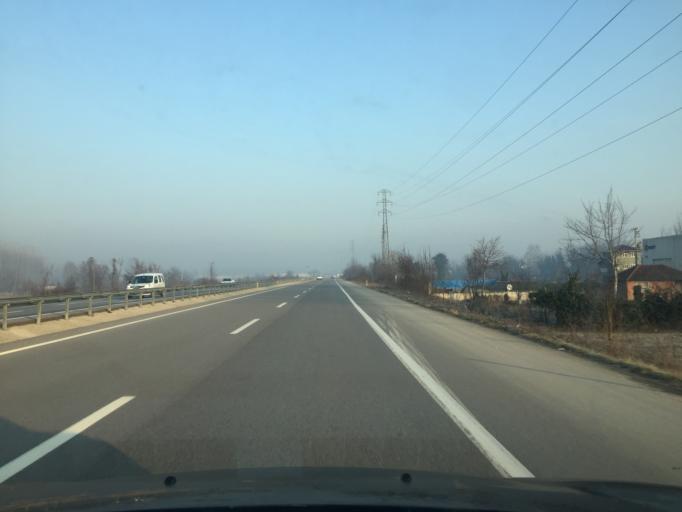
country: TR
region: Sakarya
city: Akyazi
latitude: 40.7073
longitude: 30.5661
